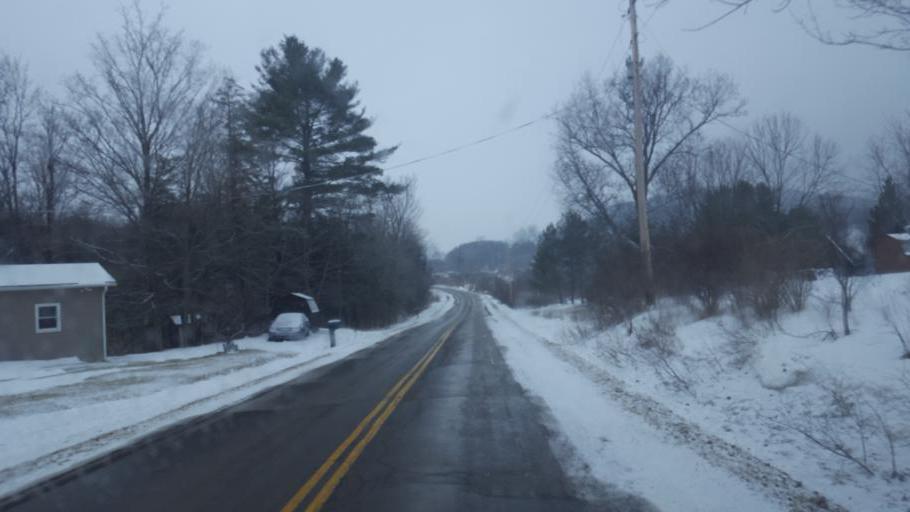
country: US
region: New York
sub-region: Steuben County
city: Canisteo
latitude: 42.1359
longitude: -77.5280
